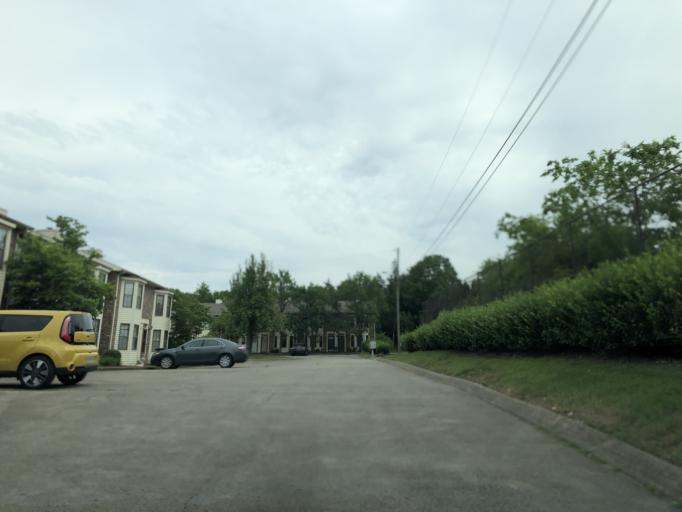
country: US
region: Tennessee
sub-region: Davidson County
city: Goodlettsville
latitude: 36.2919
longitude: -86.7083
